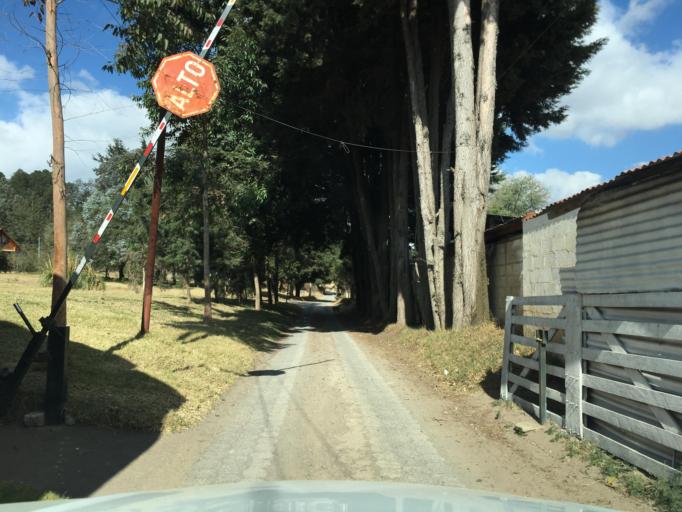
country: GT
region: Quetzaltenango
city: Quetzaltenango
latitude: 14.8432
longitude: -91.4957
